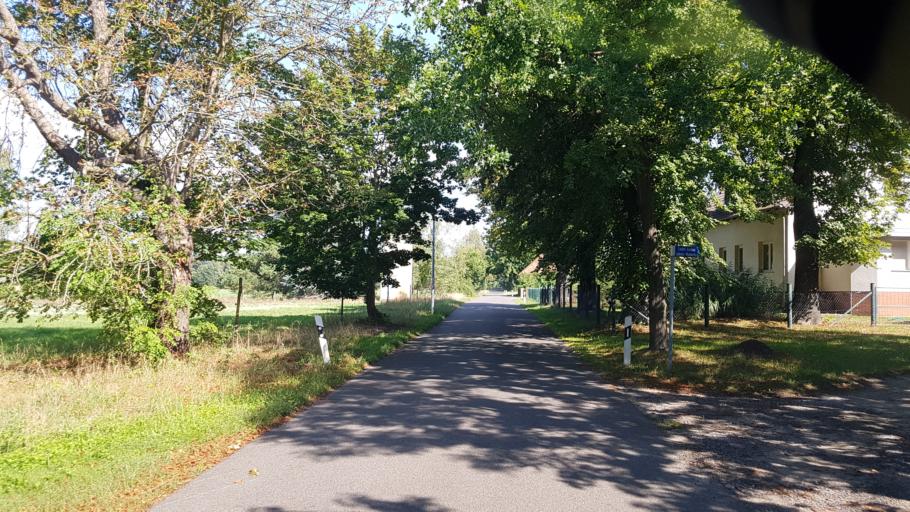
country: DE
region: Brandenburg
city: Drebkau
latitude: 51.6617
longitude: 14.2218
